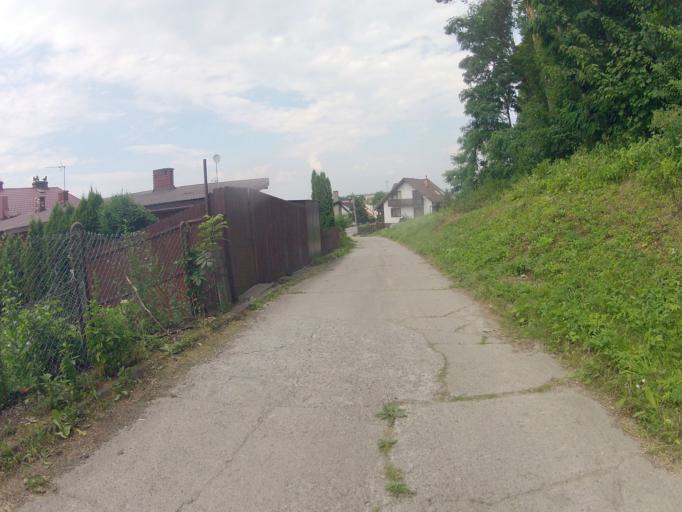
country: PL
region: Lesser Poland Voivodeship
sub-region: Powiat nowosadecki
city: Stary Sacz
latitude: 49.5647
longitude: 20.6224
